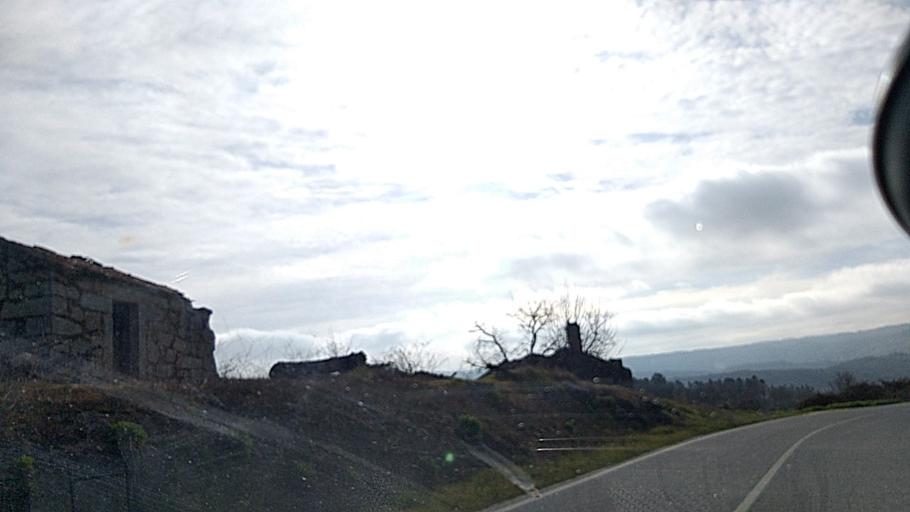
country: PT
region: Guarda
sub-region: Aguiar da Beira
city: Aguiar da Beira
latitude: 40.7453
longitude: -7.5550
